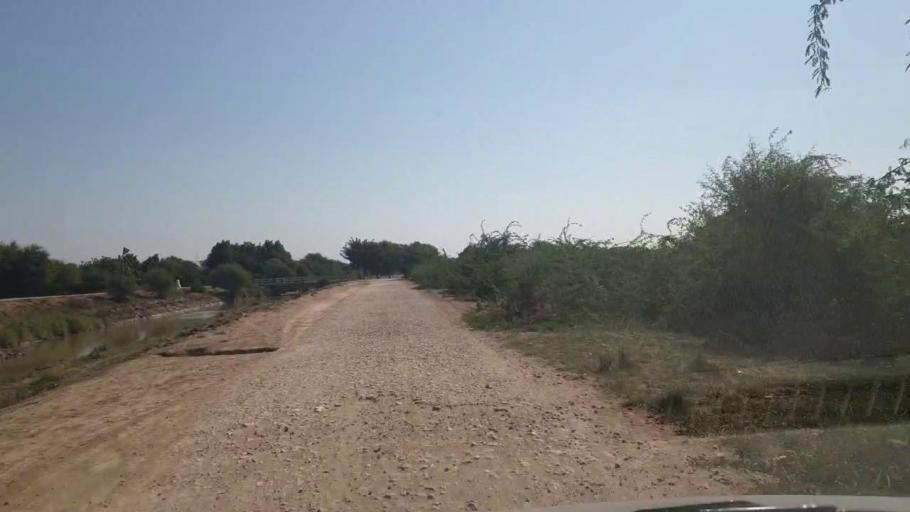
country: PK
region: Sindh
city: Digri
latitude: 24.9408
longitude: 69.1601
